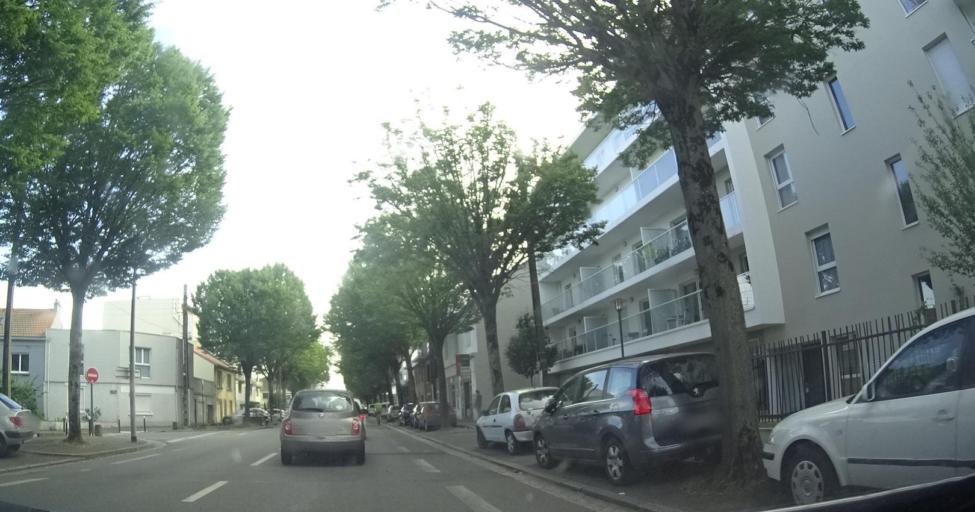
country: FR
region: Pays de la Loire
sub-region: Departement de la Loire-Atlantique
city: Nantes
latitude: 47.2452
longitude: -1.5253
